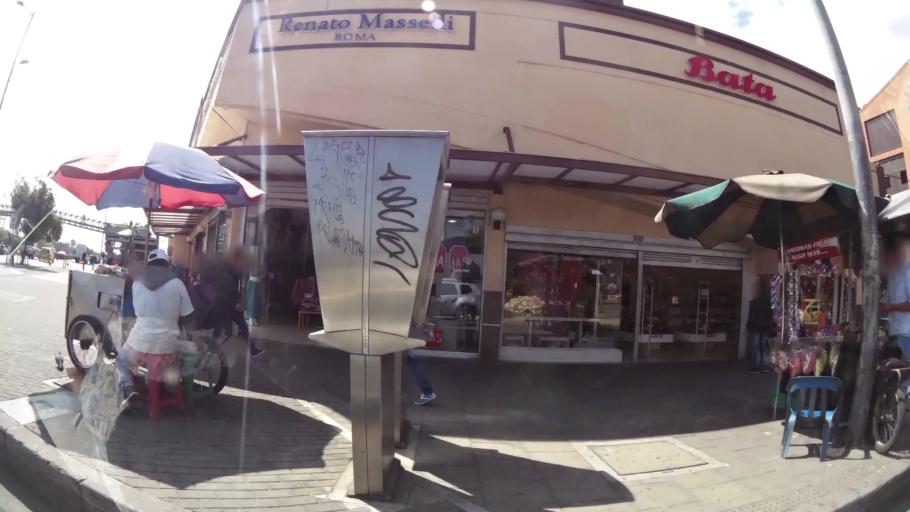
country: CO
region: Bogota D.C.
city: Bogota
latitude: 4.6288
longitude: -74.1153
